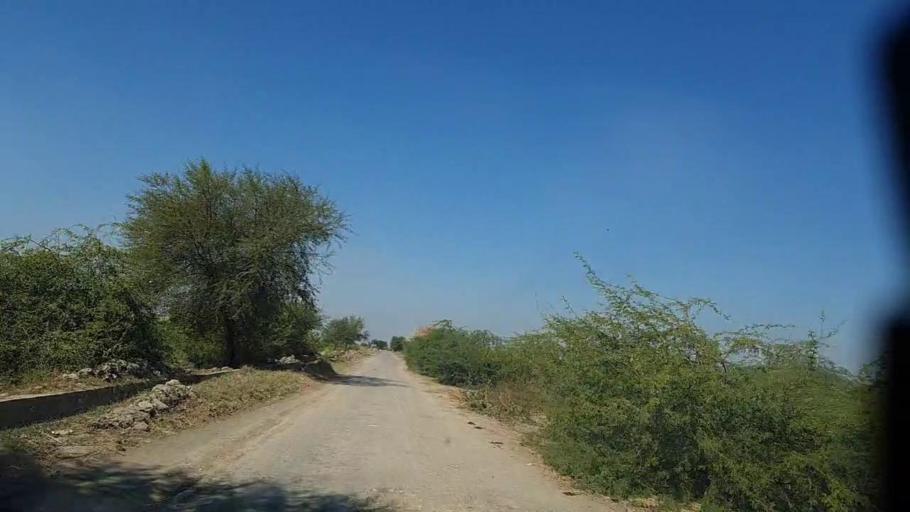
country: PK
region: Sindh
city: Digri
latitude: 25.1717
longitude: 69.0616
